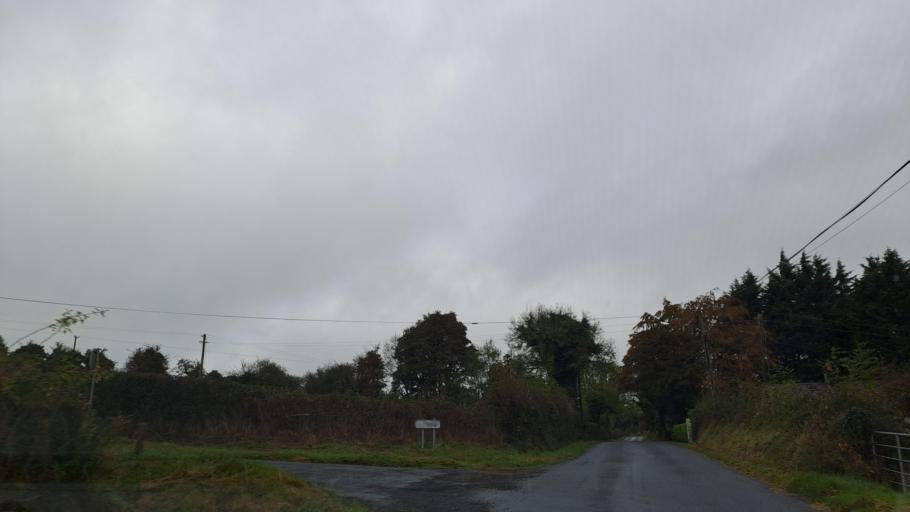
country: IE
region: Ulster
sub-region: An Cabhan
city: Bailieborough
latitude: 53.9928
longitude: -6.9441
